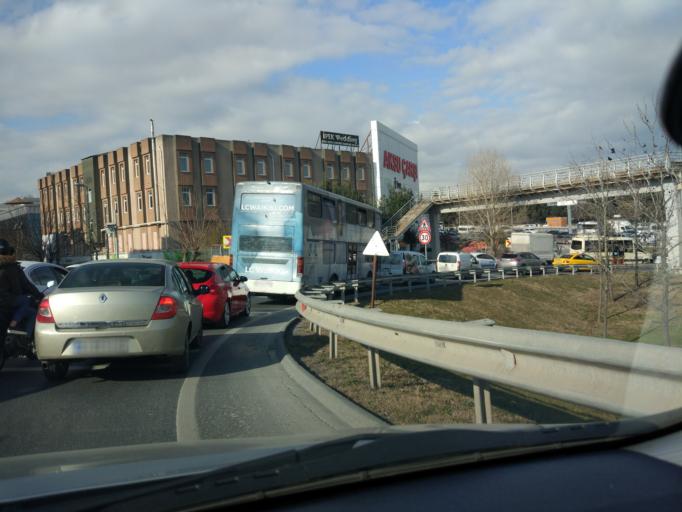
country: TR
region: Istanbul
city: Yakuplu
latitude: 40.9851
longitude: 28.7215
